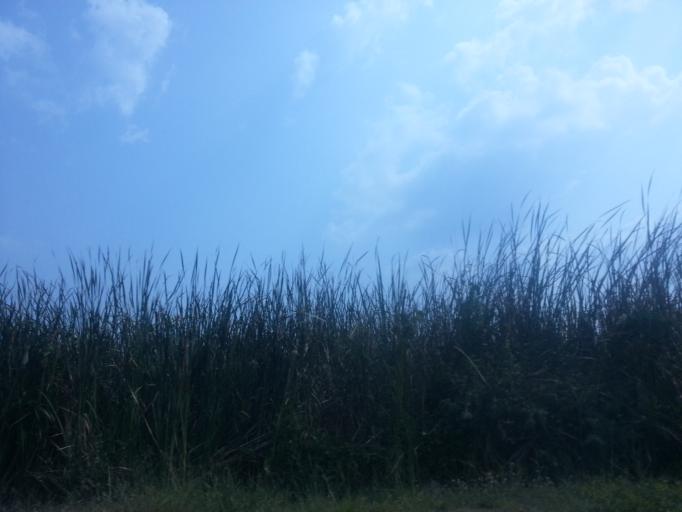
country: TH
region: Phra Nakhon Si Ayutthaya
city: Ban Bang Kadi Pathum Thani
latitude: 13.9948
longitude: 100.6167
